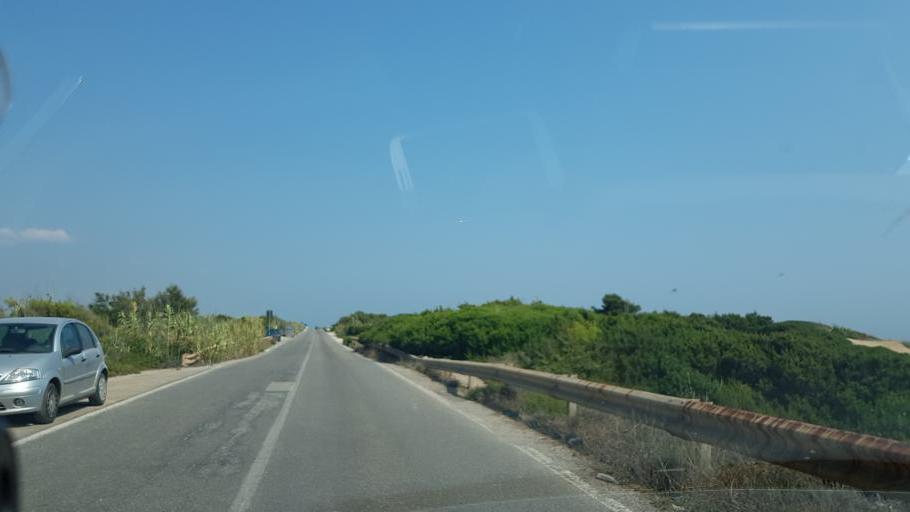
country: IT
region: Apulia
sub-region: Provincia di Taranto
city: Maruggio
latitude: 40.2994
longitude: 17.5829
